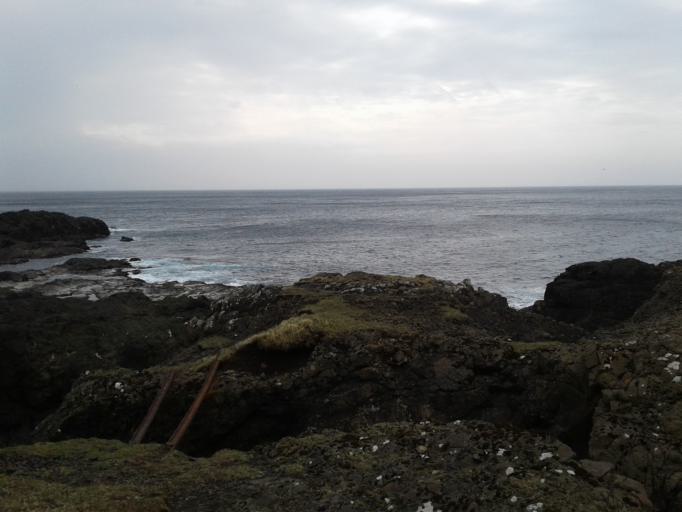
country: FO
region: Suduroy
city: Vagur
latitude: 61.4861
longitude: -6.8711
